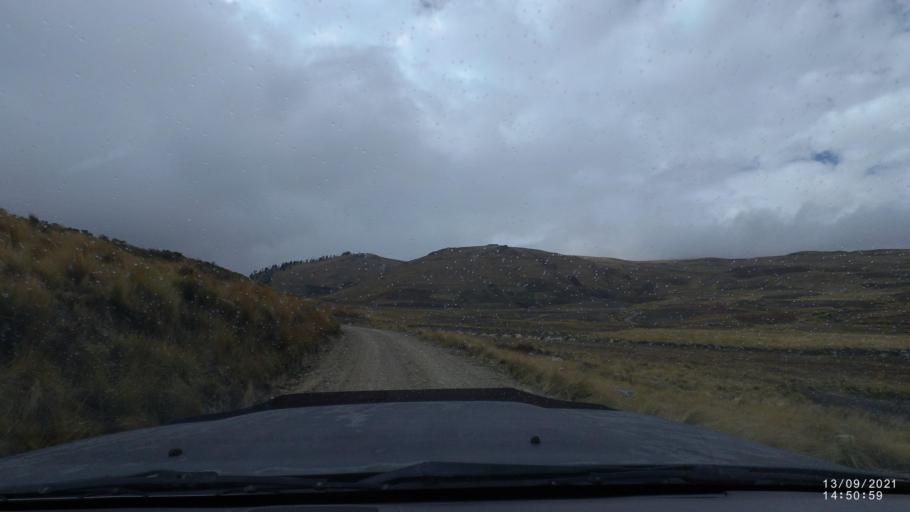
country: BO
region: Cochabamba
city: Colomi
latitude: -17.3456
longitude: -65.7924
